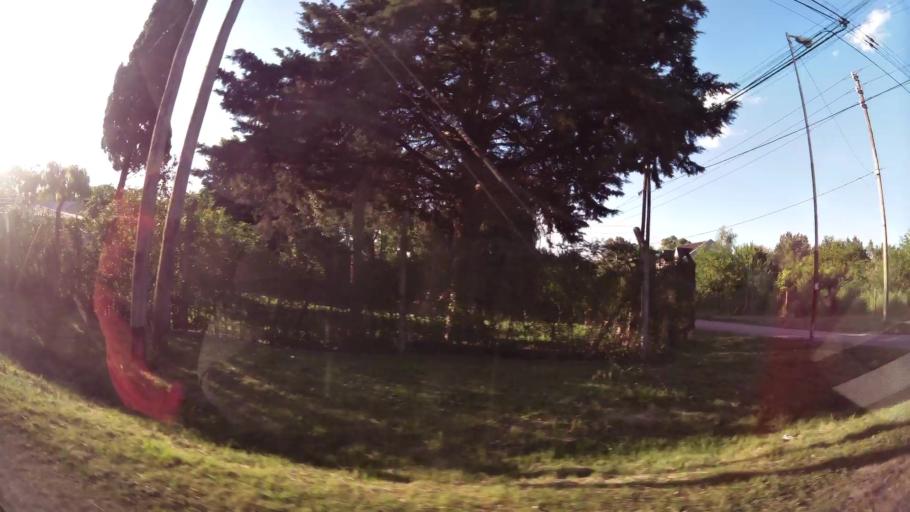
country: AR
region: Buenos Aires
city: Santa Catalina - Dique Lujan
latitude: -34.4672
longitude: -58.7455
